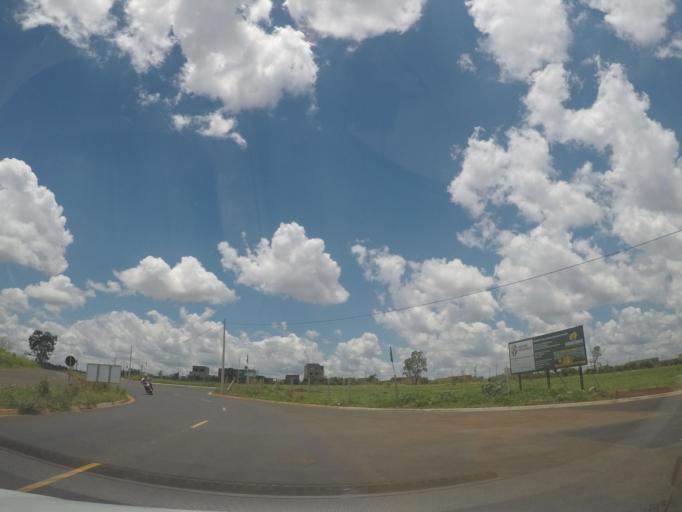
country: BR
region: Sao Paulo
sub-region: Hortolandia
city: Hortolandia
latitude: -22.8365
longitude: -47.2183
